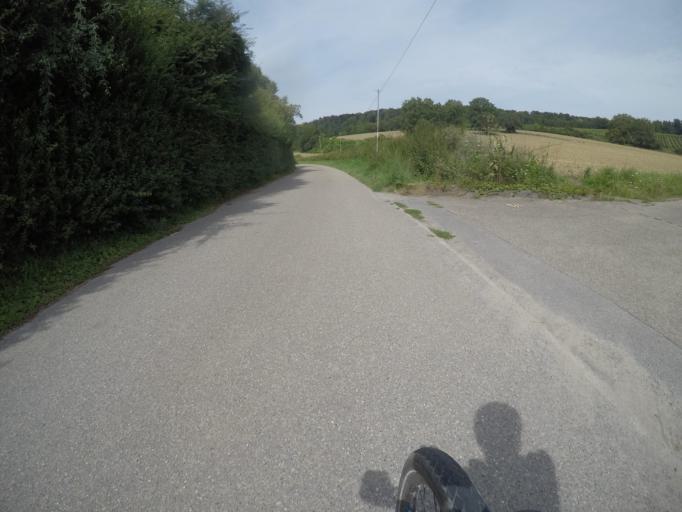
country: DE
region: Baden-Wuerttemberg
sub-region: Karlsruhe Region
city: Bruchsal
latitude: 49.1139
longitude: 8.6376
